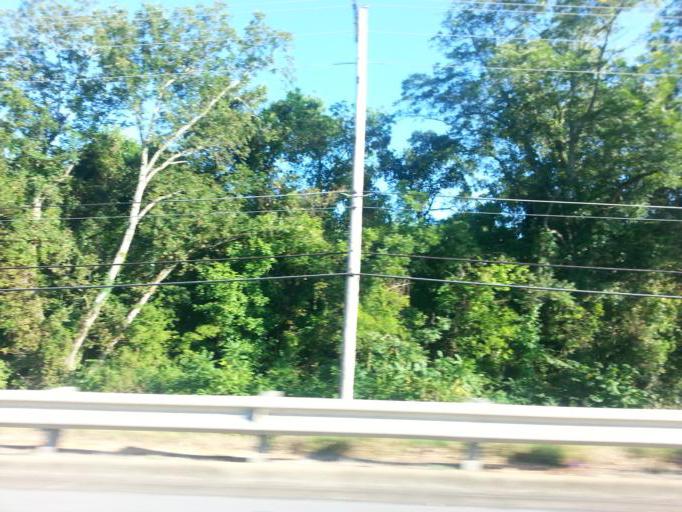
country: US
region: Alabama
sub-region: Lauderdale County
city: East Florence
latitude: 34.8261
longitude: -87.6426
